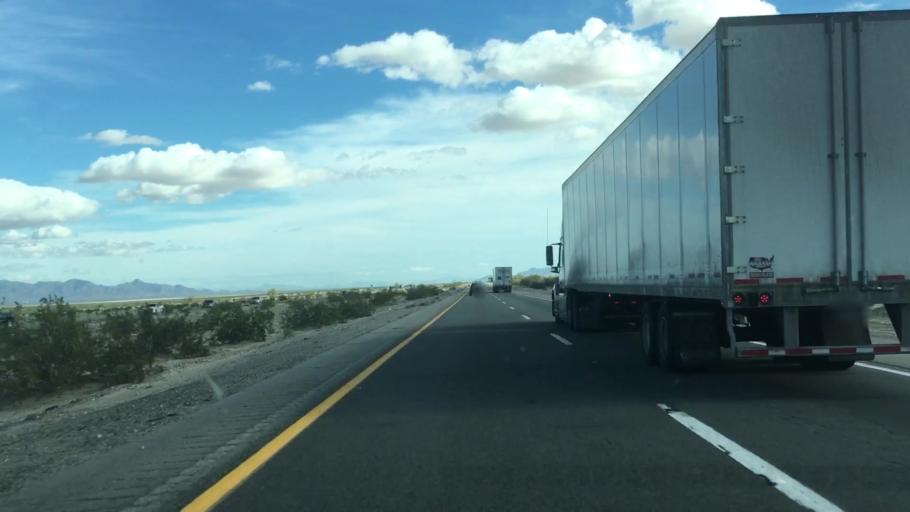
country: US
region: California
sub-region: Riverside County
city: Mesa Verde
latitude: 33.6469
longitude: -115.1236
